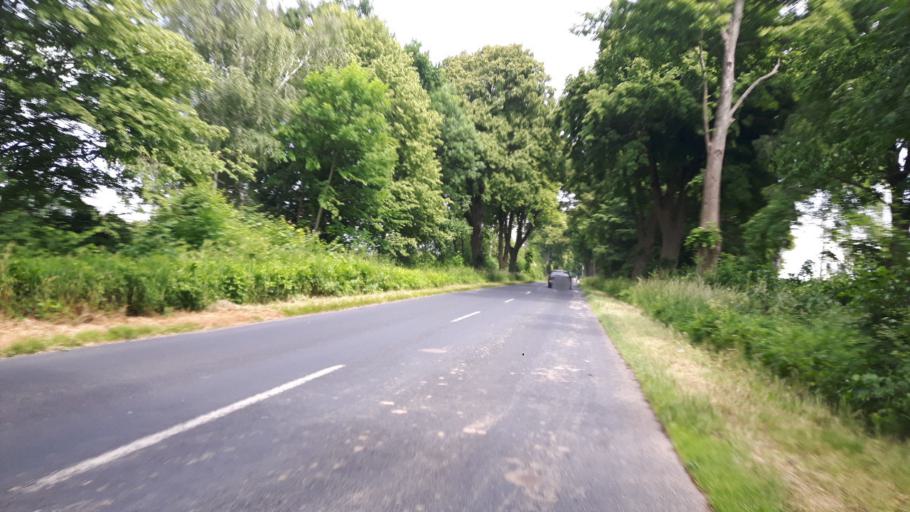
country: PL
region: Warmian-Masurian Voivodeship
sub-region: Powiat braniewski
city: Braniewo
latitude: 54.3635
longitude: 19.7572
